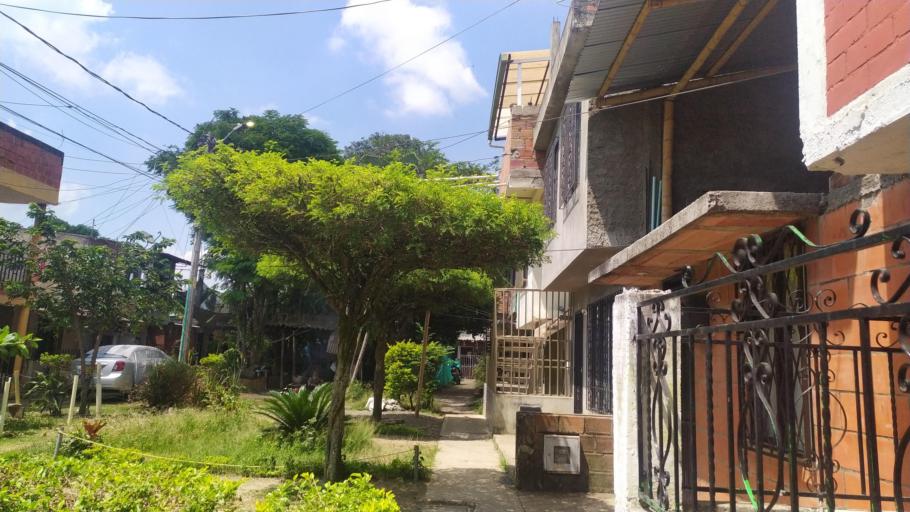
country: CO
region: Valle del Cauca
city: Jamundi
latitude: 3.2493
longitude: -76.5421
